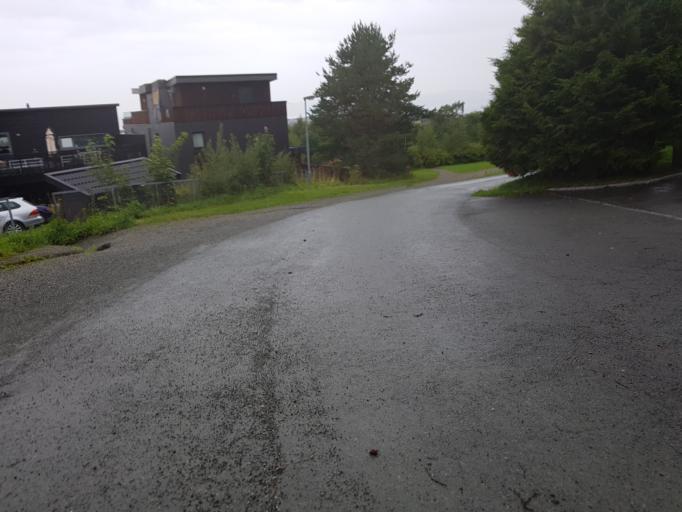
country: NO
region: Sor-Trondelag
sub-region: Trondheim
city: Trondheim
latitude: 63.4068
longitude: 10.4539
